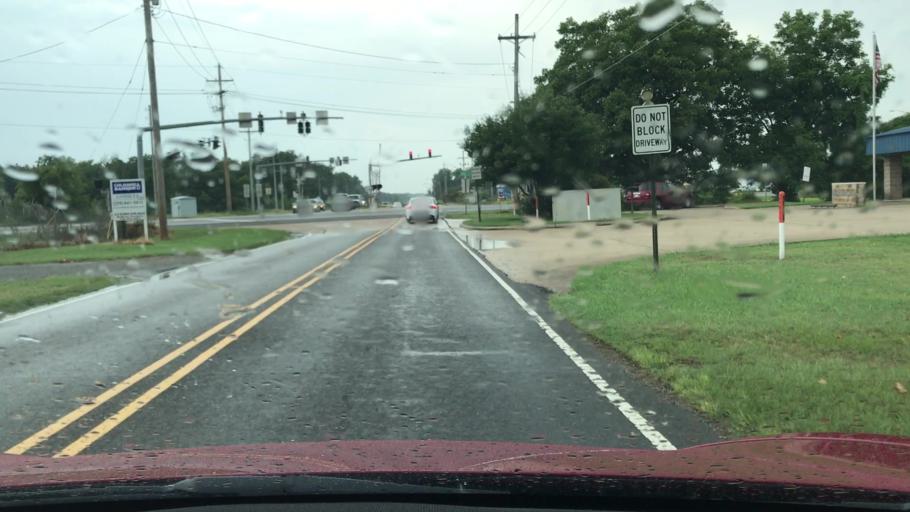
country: US
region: Louisiana
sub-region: Bossier Parish
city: Bossier City
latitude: 32.4009
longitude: -93.6925
